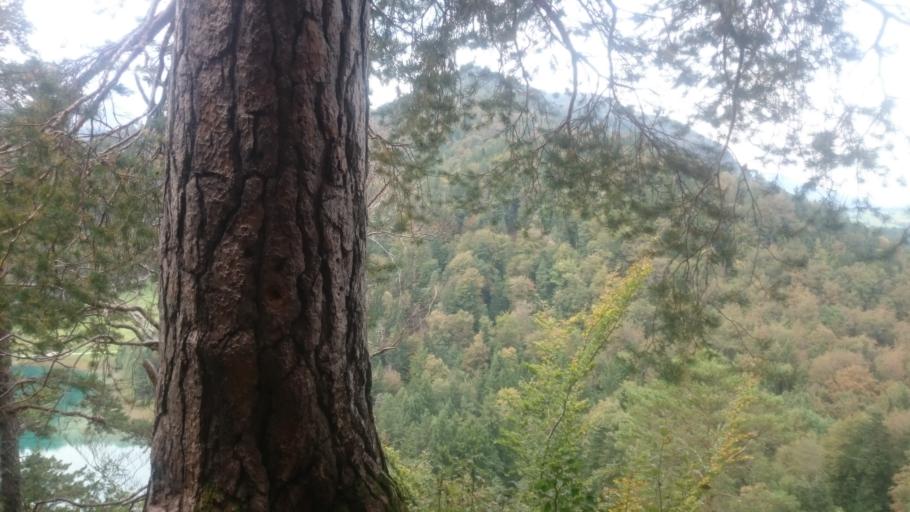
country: AT
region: Tyrol
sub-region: Politischer Bezirk Reutte
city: Vils
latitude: 47.5631
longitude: 10.6418
